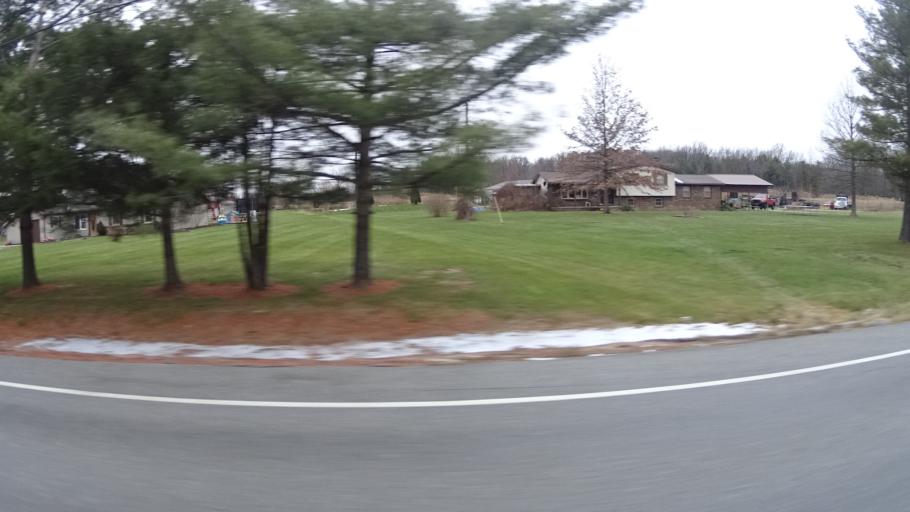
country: US
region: Ohio
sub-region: Lorain County
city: Eaton Estates
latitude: 41.3027
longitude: -82.0014
